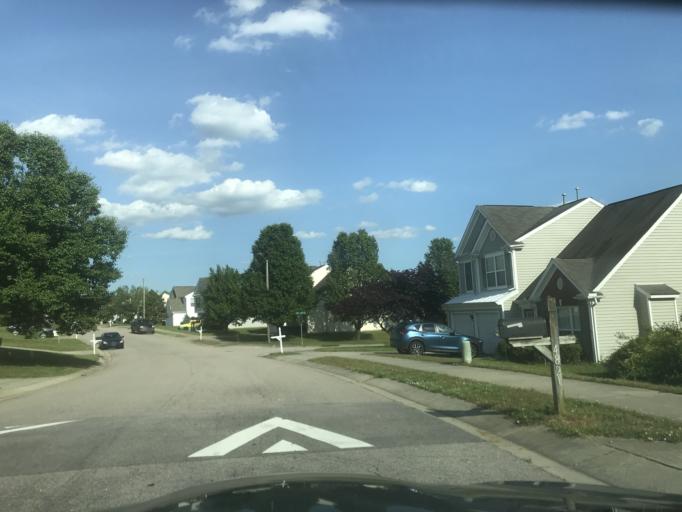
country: US
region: North Carolina
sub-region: Wake County
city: Knightdale
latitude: 35.8436
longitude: -78.5505
